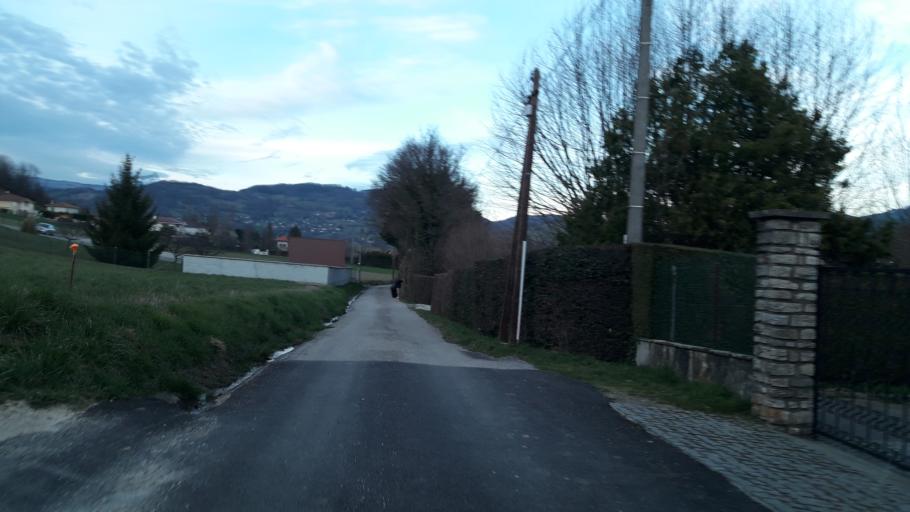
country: FR
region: Rhone-Alpes
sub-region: Departement de l'Isere
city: Brie-et-Angonnes
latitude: 45.1101
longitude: 5.7832
